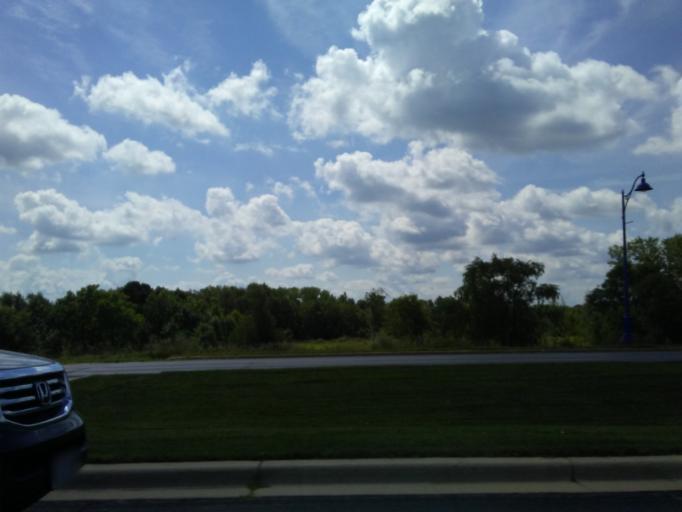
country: US
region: Wisconsin
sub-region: Dane County
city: Verona
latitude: 42.9945
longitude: -89.5160
